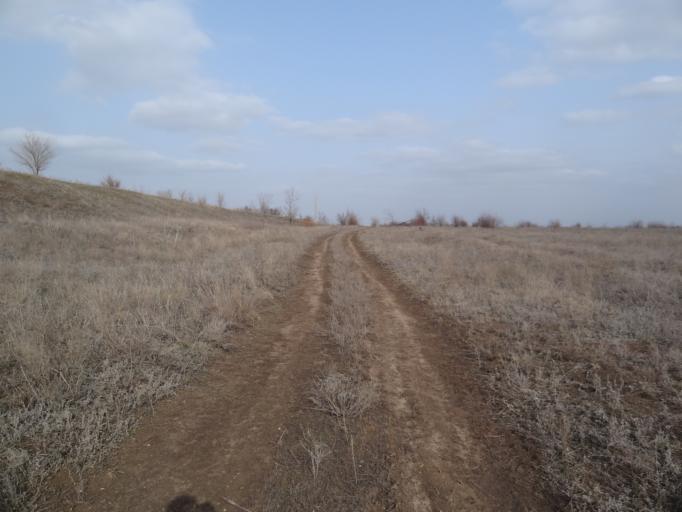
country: RU
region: Saratov
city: Shumeyka
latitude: 51.4714
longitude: 46.2909
